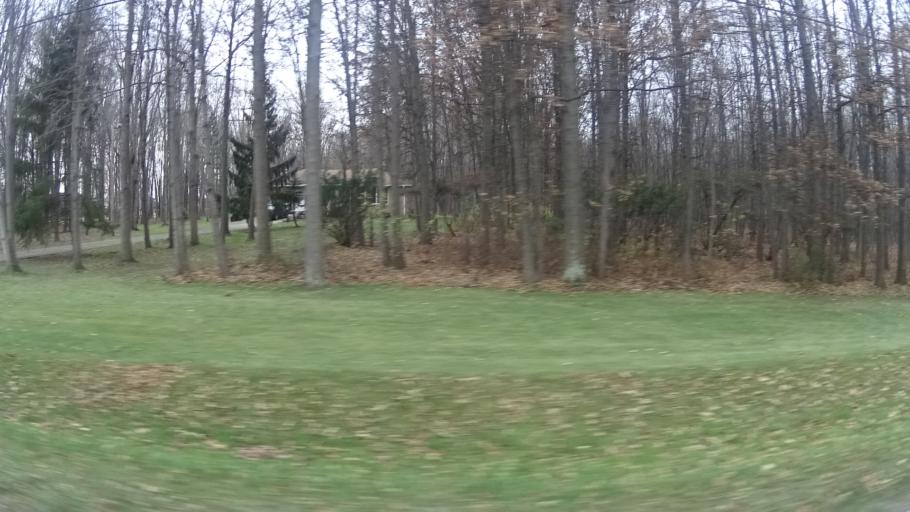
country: US
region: Ohio
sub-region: Cuyahoga County
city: Olmsted Falls
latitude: 41.3420
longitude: -81.9429
